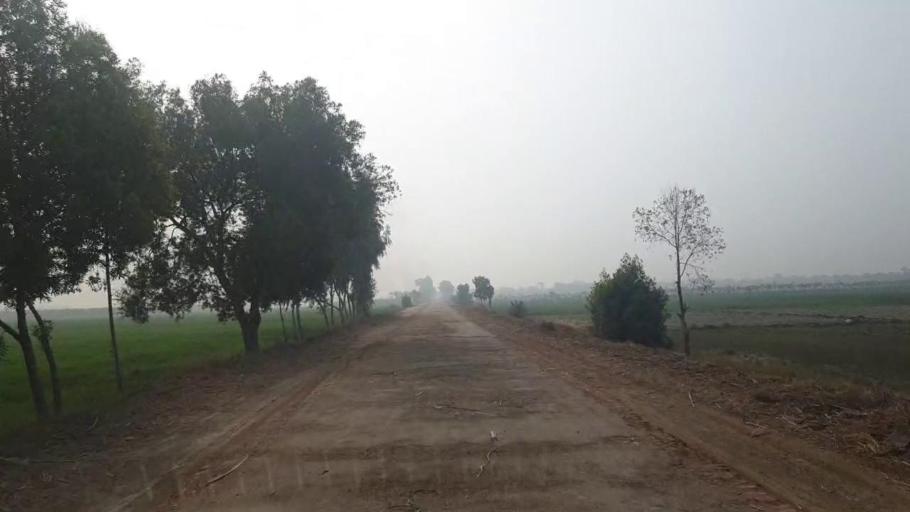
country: PK
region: Sindh
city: Tando Adam
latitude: 25.7746
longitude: 68.6073
